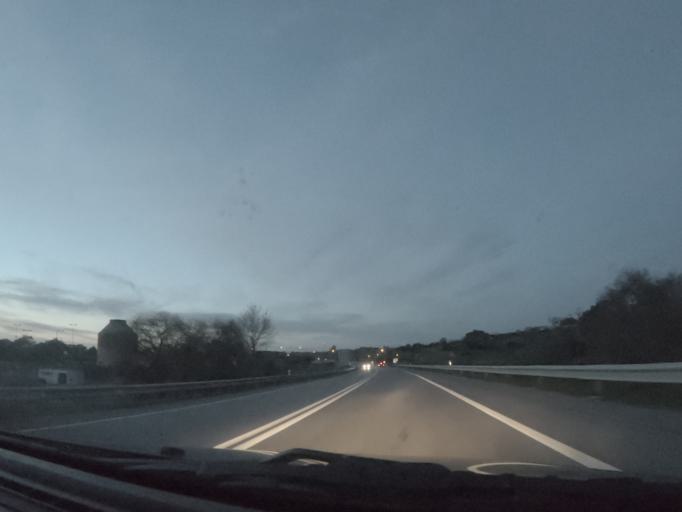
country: PT
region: Castelo Branco
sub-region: Castelo Branco
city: Castelo Branco
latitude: 39.8476
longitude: -7.5000
